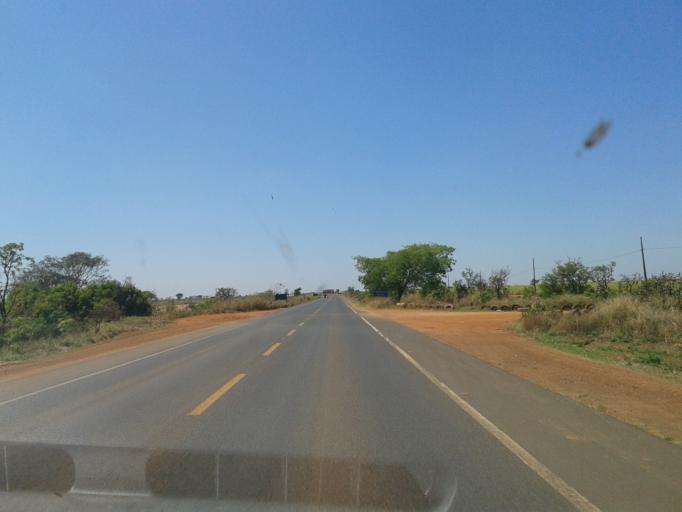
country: BR
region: Minas Gerais
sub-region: Sacramento
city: Sacramento
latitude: -19.3204
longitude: -47.5638
